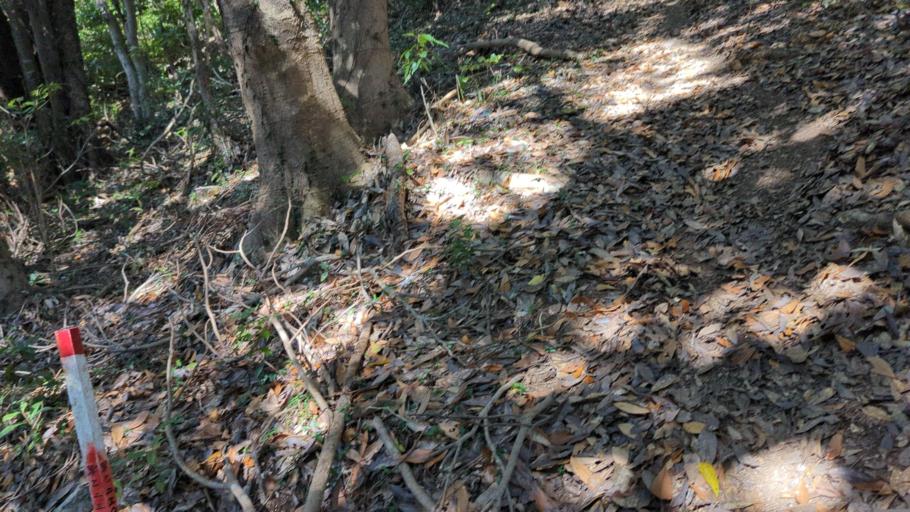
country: JP
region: Aichi
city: Toyohashi
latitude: 34.7700
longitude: 137.4508
